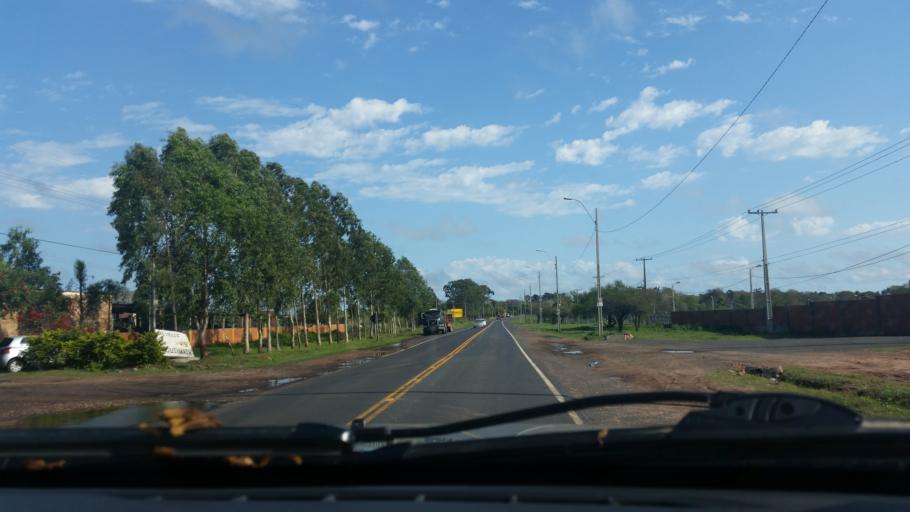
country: PY
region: Presidente Hayes
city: Villa Hayes
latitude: -25.0458
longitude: -57.5439
